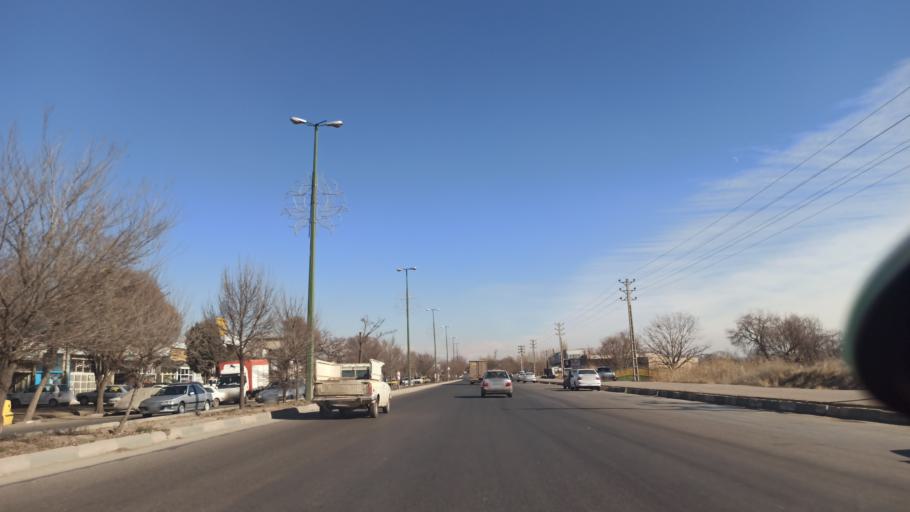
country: IR
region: Qazvin
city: Qazvin
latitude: 36.2563
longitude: 49.9810
